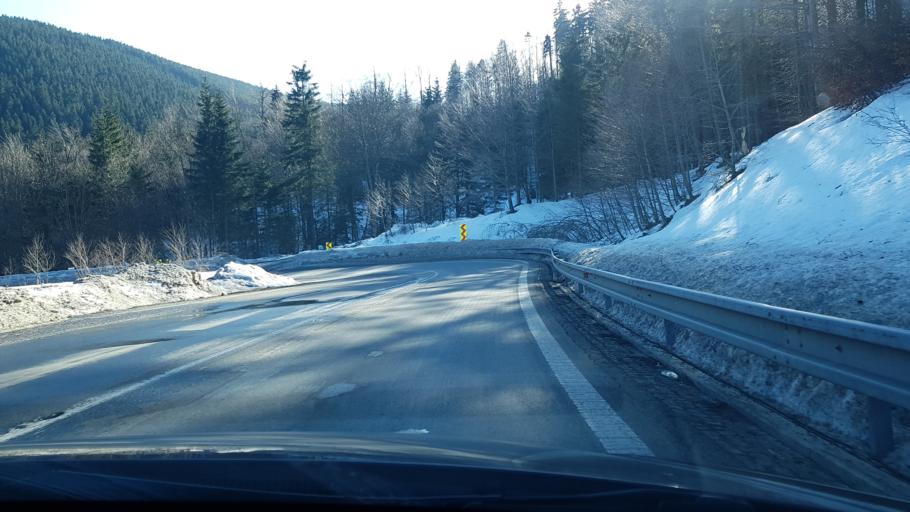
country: CZ
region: Olomoucky
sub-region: Okres Sumperk
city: Loucna nad Desnou
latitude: 50.1344
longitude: 17.1629
